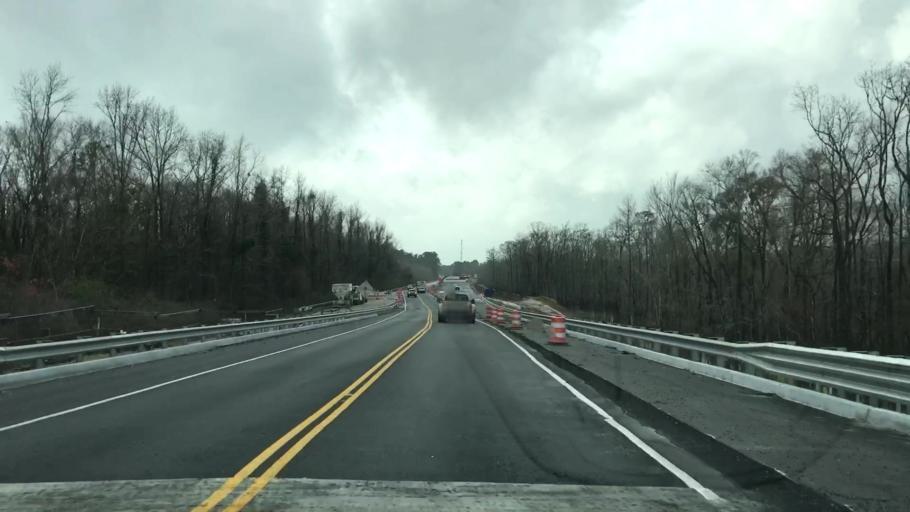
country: US
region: South Carolina
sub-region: Georgetown County
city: Murrells Inlet
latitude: 33.6594
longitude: -79.1561
